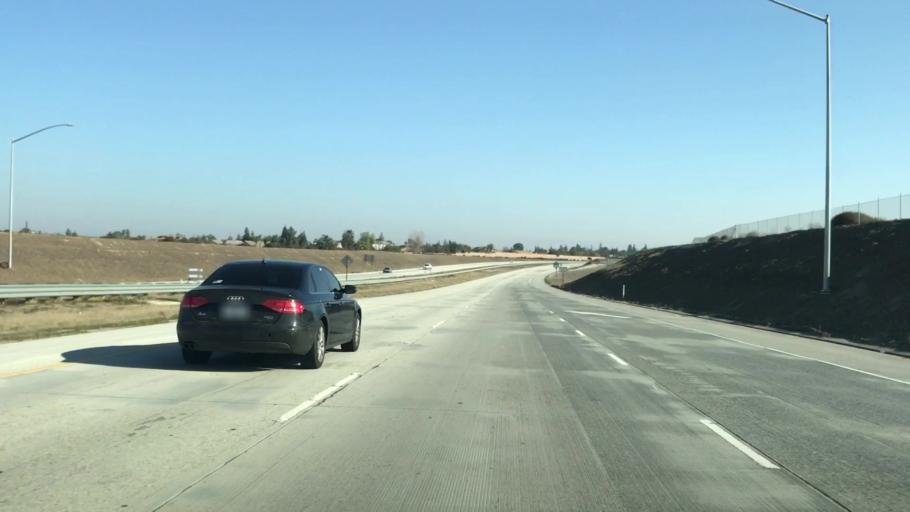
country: US
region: California
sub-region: Kern County
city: Rosedale
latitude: 35.3561
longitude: -119.1738
